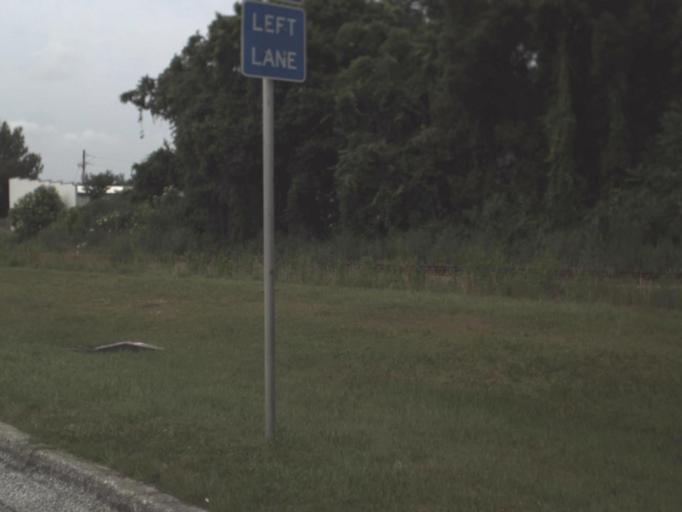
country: US
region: Florida
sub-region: Duval County
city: Jacksonville
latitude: 30.2850
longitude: -81.7204
